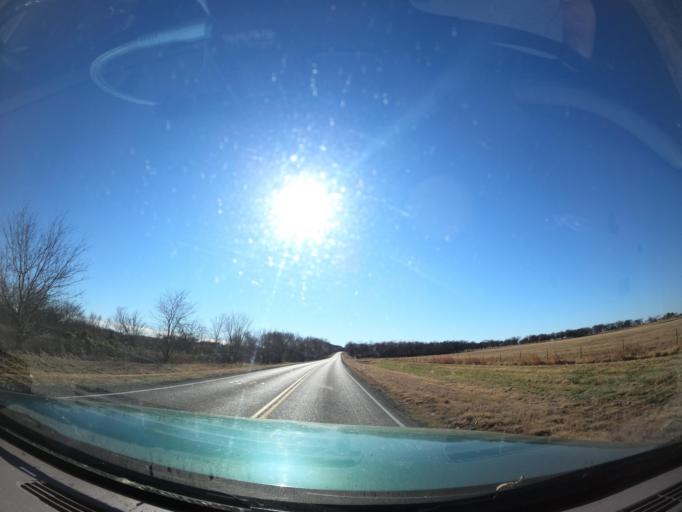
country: US
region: Oklahoma
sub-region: Muskogee County
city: Haskell
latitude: 35.6648
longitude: -95.6439
